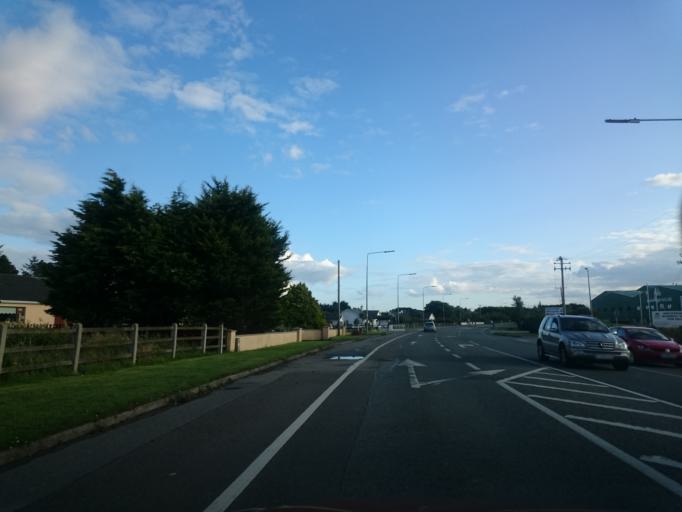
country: IE
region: Leinster
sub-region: Loch Garman
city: Ballygerry
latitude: 52.2453
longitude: -6.3460
